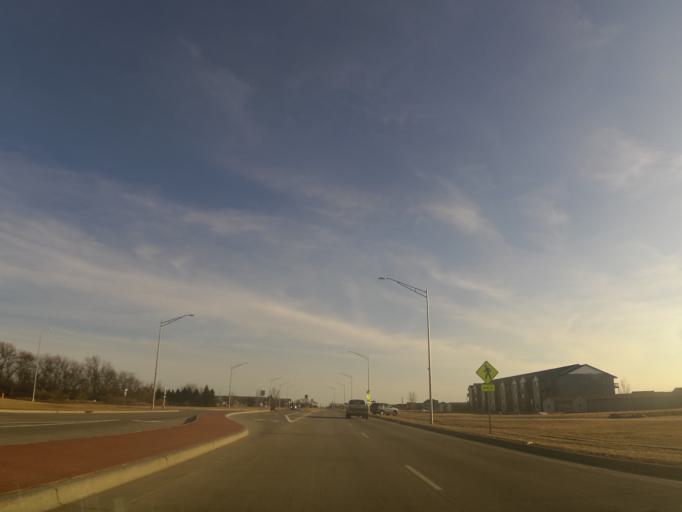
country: US
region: North Dakota
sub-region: Grand Forks County
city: Grand Forks
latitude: 47.8743
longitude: -97.0455
